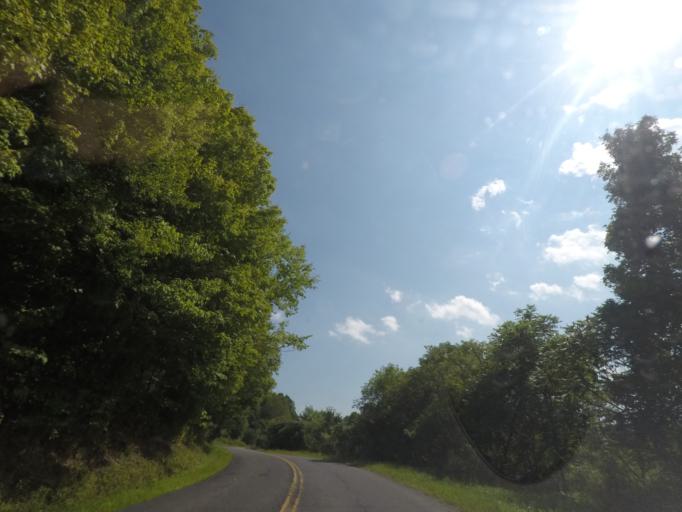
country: US
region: New York
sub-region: Saratoga County
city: Waterford
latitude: 42.8097
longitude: -73.5925
